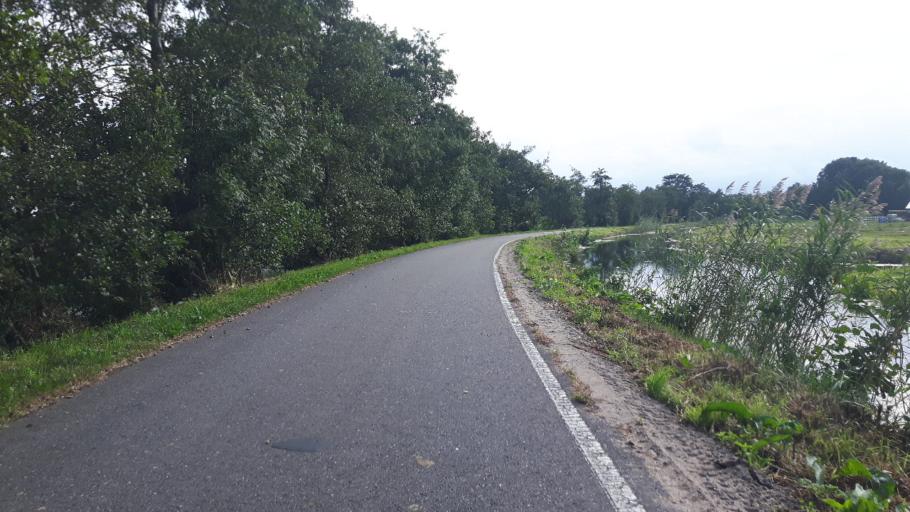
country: NL
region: Utrecht
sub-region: Gemeente De Ronde Venen
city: Mijdrecht
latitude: 52.1659
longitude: 4.9014
